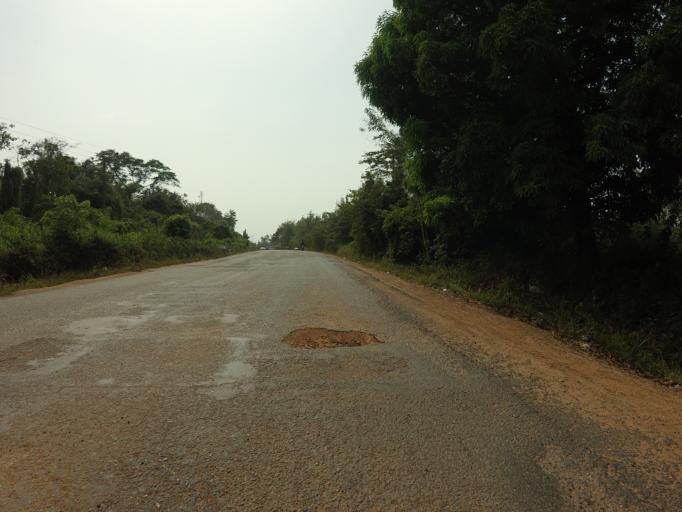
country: GH
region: Volta
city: Ho
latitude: 6.3803
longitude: 0.1867
